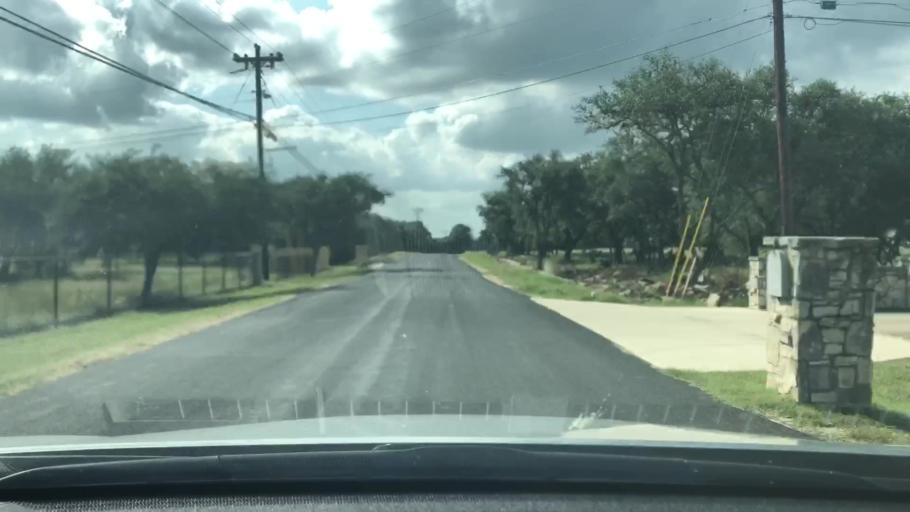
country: US
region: Texas
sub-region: Bexar County
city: Fair Oaks Ranch
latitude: 29.7675
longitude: -98.6280
